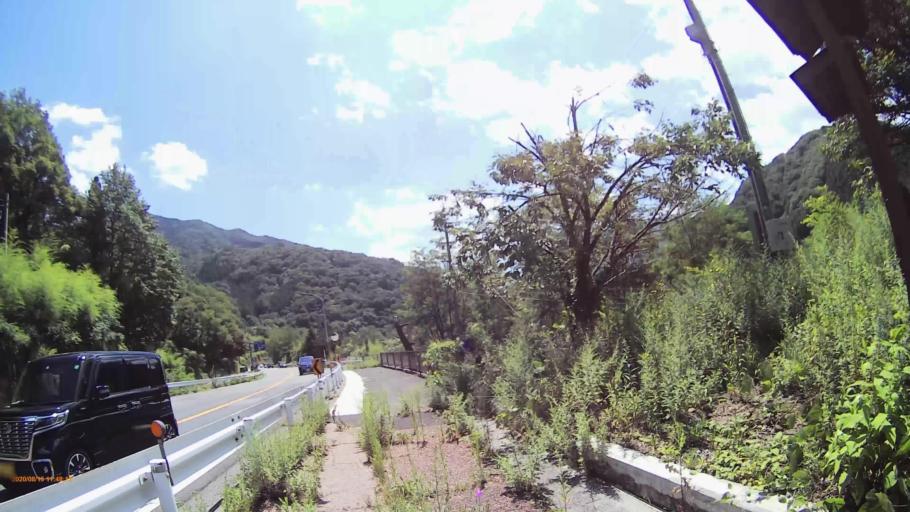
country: JP
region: Nagano
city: Ina
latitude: 35.8300
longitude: 137.6821
